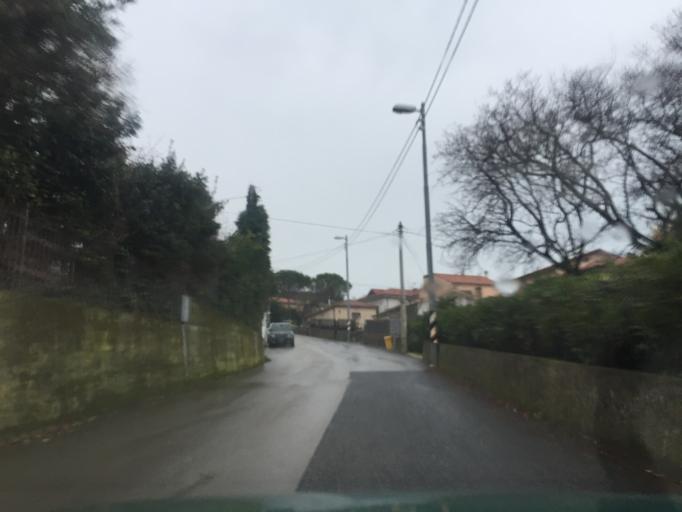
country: IT
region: Friuli Venezia Giulia
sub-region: Provincia di Trieste
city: Muggia
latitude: 45.6031
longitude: 13.7582
